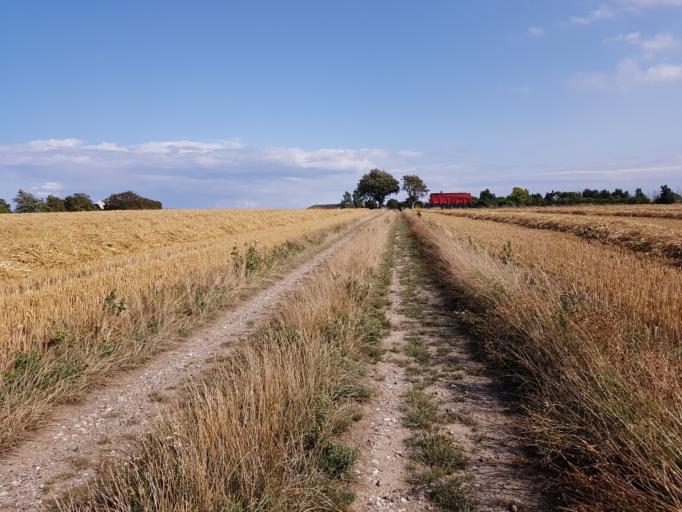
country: DK
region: Zealand
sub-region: Guldborgsund Kommune
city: Nykobing Falster
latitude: 54.5878
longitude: 11.9387
